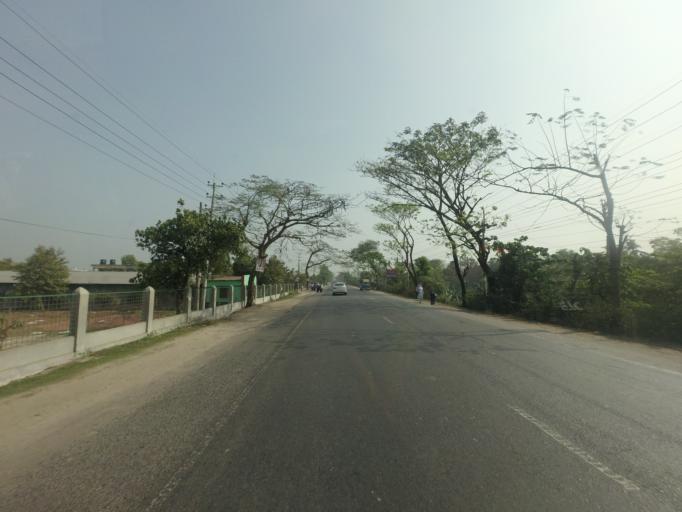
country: BD
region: Dhaka
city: Narsingdi
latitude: 23.8288
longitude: 90.6085
